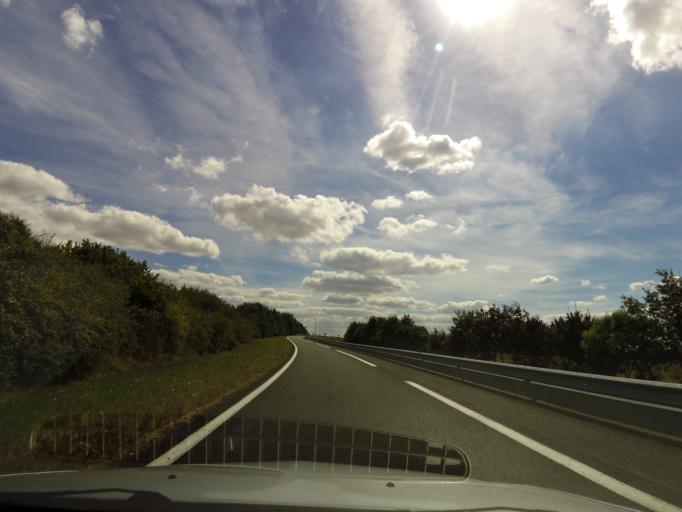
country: FR
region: Pays de la Loire
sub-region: Departement de la Vendee
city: Les Essarts
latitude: 46.8096
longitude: -1.2110
